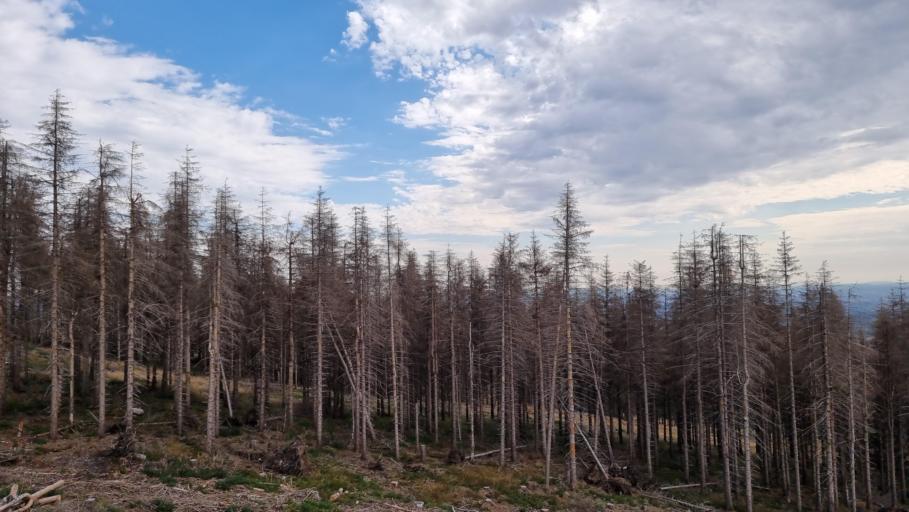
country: DE
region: Lower Saxony
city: Braunlage
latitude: 51.7525
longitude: 10.6173
